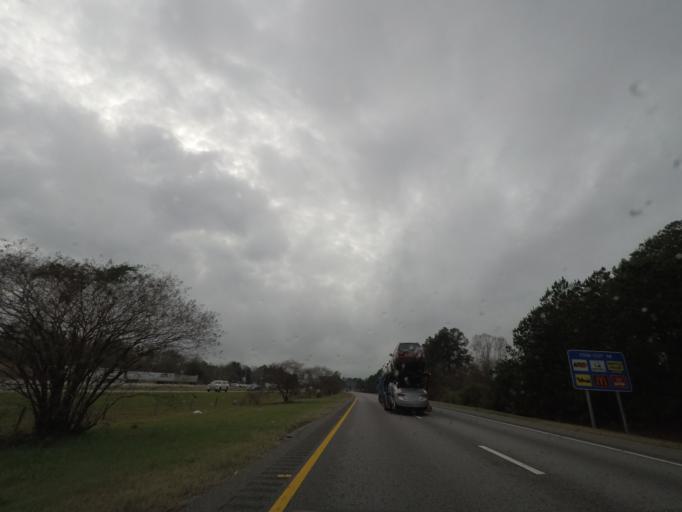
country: US
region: South Carolina
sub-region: Orangeburg County
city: Holly Hill
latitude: 33.4976
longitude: -80.4628
